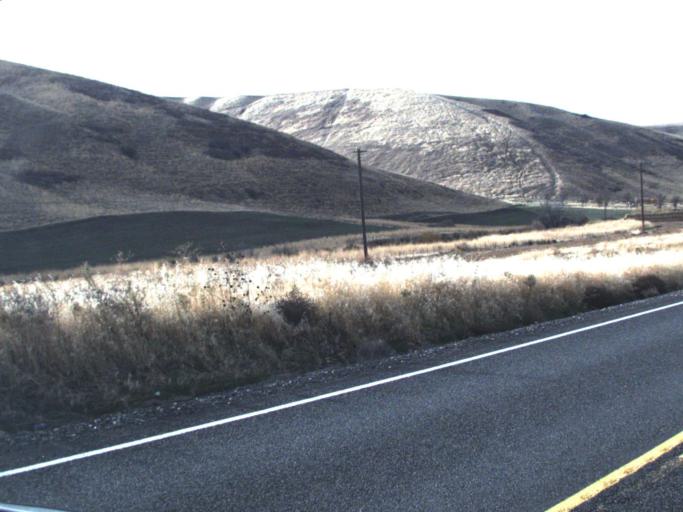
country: US
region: Washington
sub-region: Garfield County
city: Pomeroy
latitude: 46.4875
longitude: -117.7561
